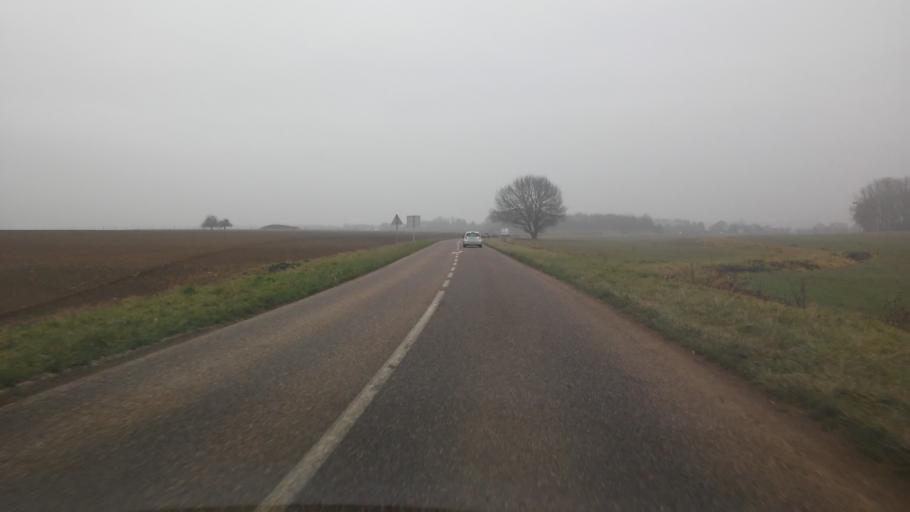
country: FR
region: Lorraine
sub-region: Departement de la Moselle
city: Augny
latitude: 49.0569
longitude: 6.1256
